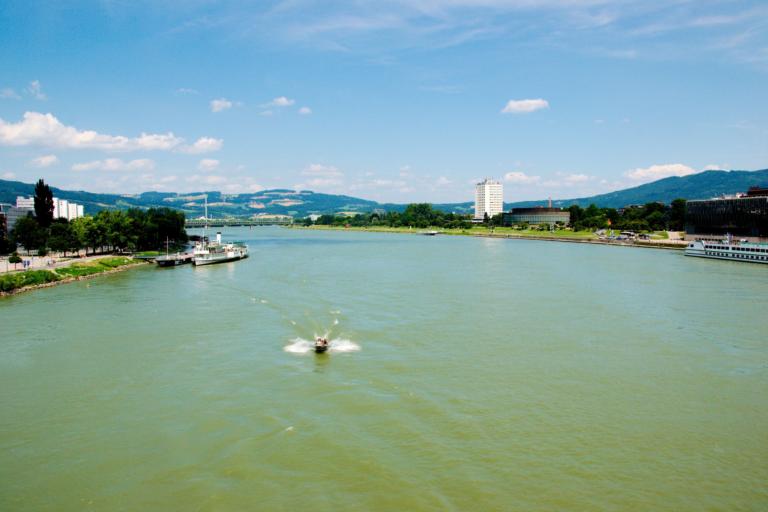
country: AT
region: Upper Austria
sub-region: Linz Stadt
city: Linz
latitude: 48.3086
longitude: 14.2848
